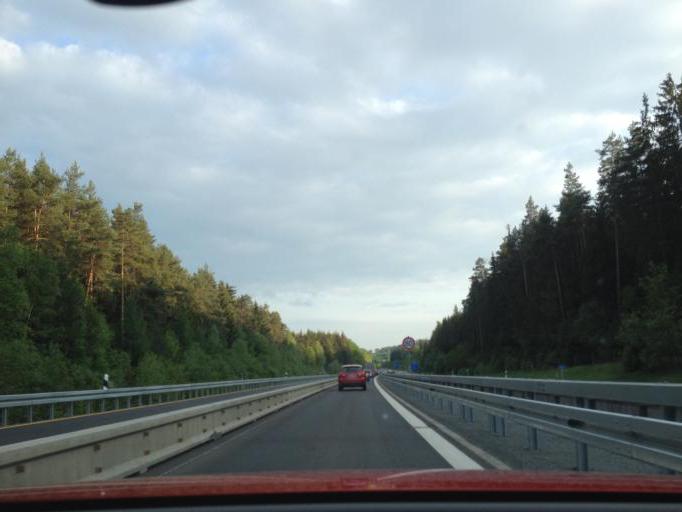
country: DE
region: Bavaria
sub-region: Upper Palatinate
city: Neustadt an der Waldnaab
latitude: 49.7533
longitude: 12.1541
